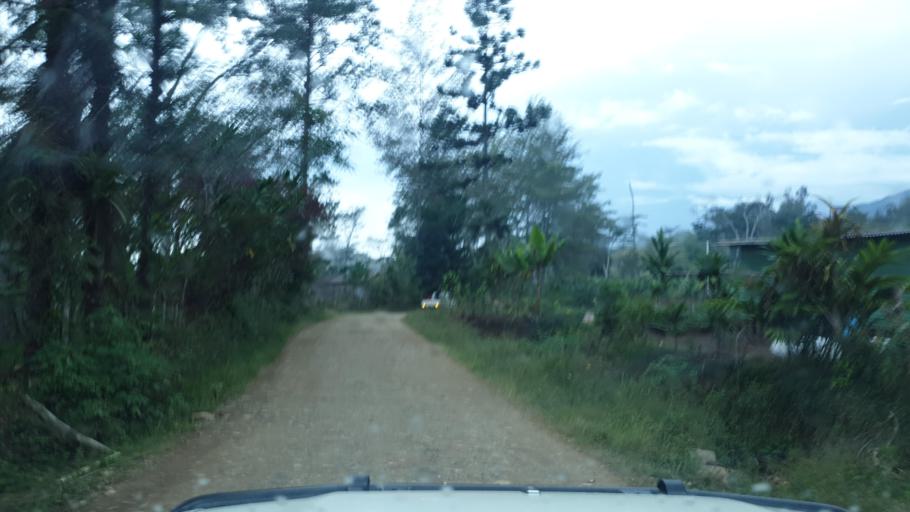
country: PG
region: Eastern Highlands
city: Goroka
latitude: -5.9840
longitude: 145.2826
